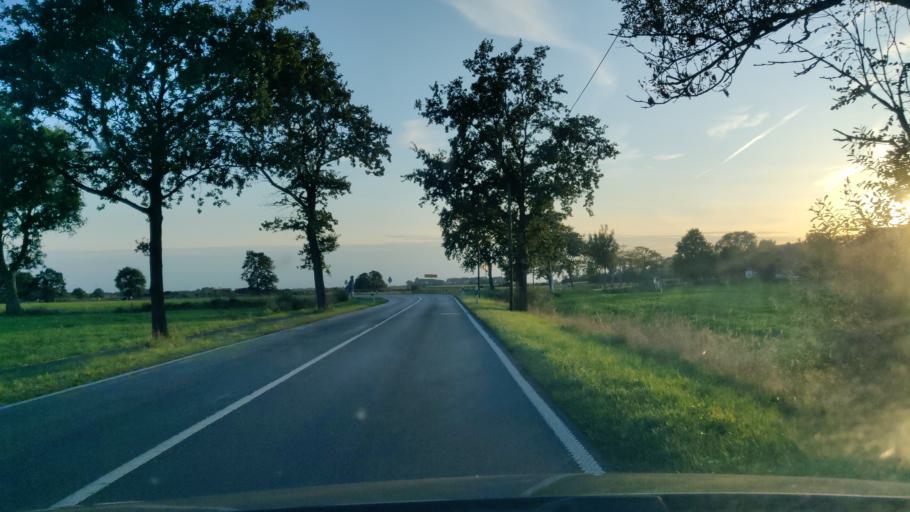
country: DE
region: Lower Saxony
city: Aurich
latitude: 53.4375
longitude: 7.3916
